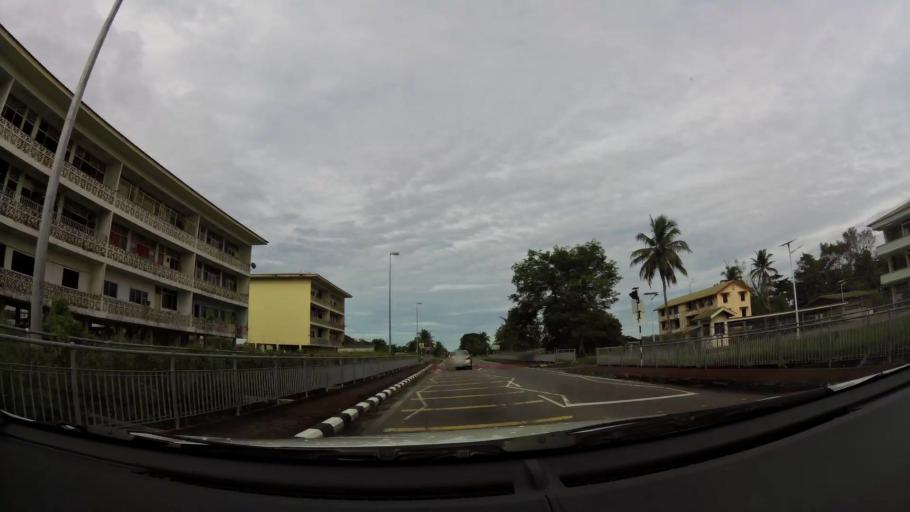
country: BN
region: Belait
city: Seria
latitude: 4.6111
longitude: 114.3283
